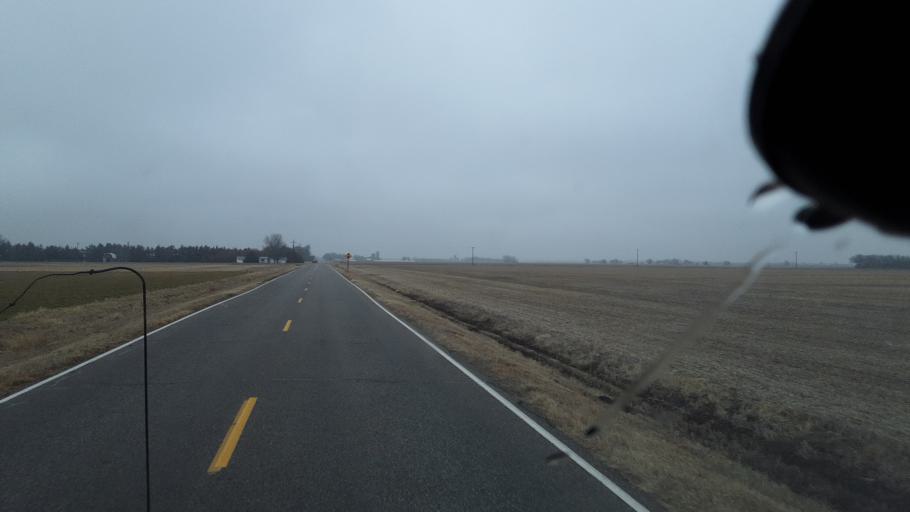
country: US
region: Kansas
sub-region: Reno County
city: South Hutchinson
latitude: 37.9667
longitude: -98.0138
